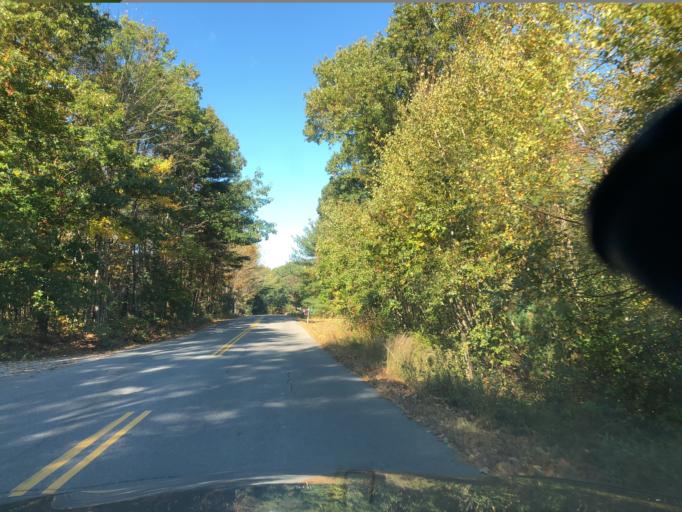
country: US
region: New Hampshire
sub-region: Strafford County
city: Lee
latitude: 43.1201
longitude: -70.9781
